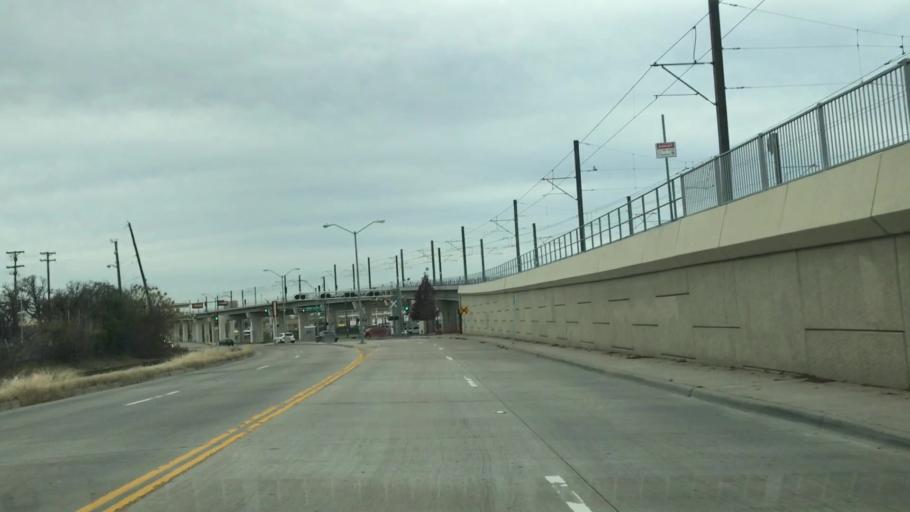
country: US
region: Texas
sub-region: Dallas County
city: Farmers Branch
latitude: 32.8533
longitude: -96.8770
